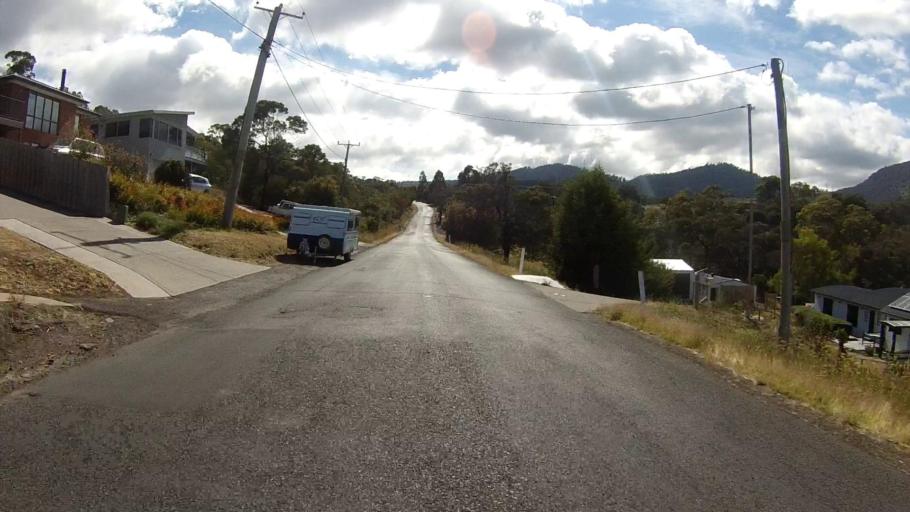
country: AU
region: Tasmania
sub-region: Brighton
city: Old Beach
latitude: -42.7761
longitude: 147.2837
